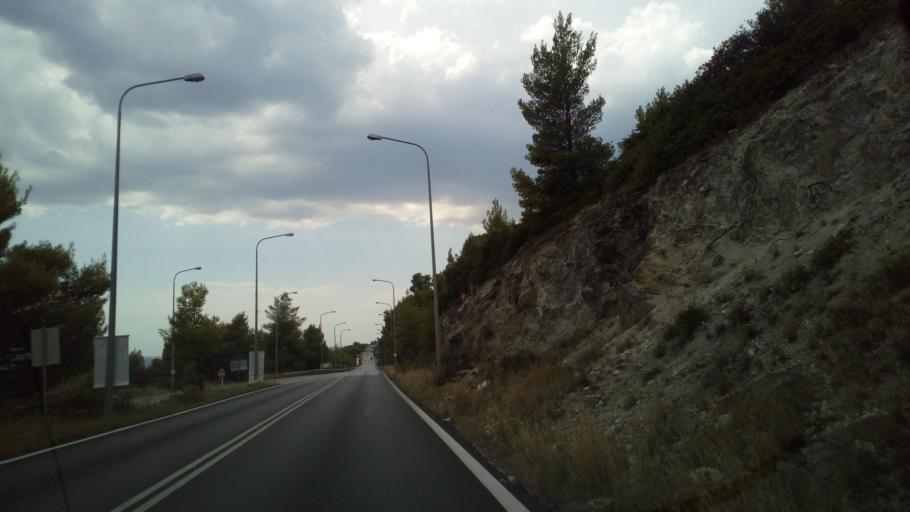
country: GR
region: Central Macedonia
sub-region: Nomos Chalkidikis
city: Ormylia
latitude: 40.2609
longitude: 23.4865
